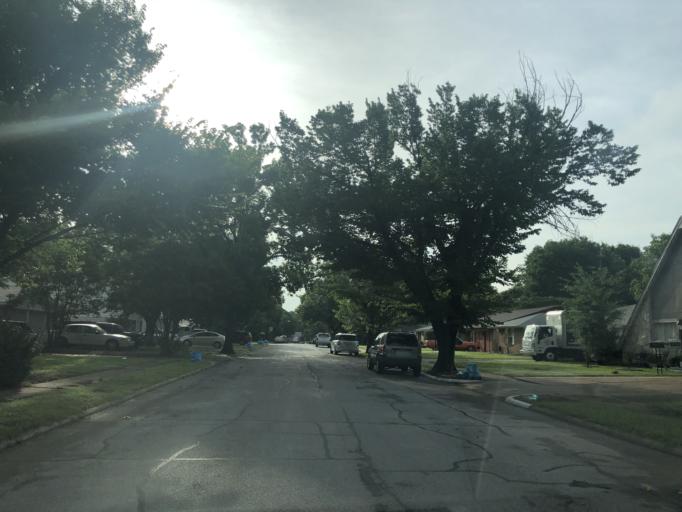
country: US
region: Texas
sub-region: Dallas County
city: Irving
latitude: 32.8048
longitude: -96.9747
